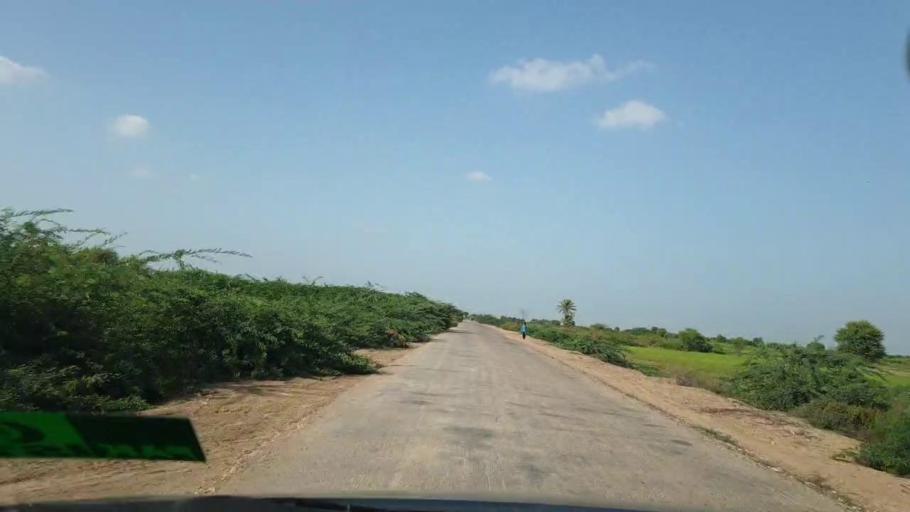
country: PK
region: Sindh
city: Tando Bago
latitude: 24.7130
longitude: 69.1930
